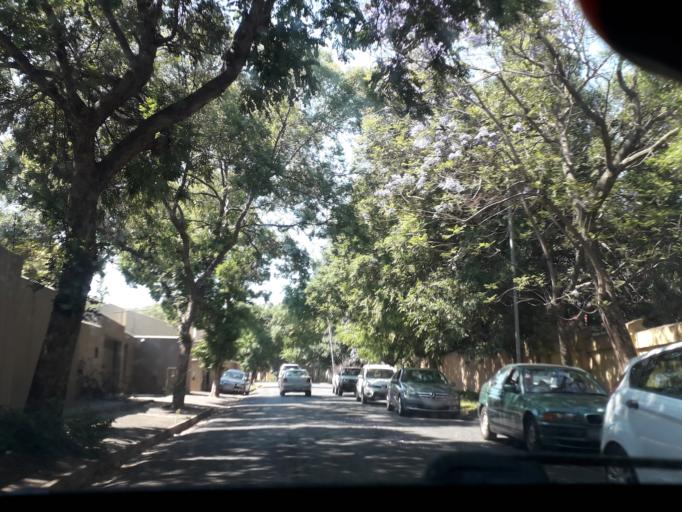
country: ZA
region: Gauteng
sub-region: City of Johannesburg Metropolitan Municipality
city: Johannesburg
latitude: -26.1483
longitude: 28.0627
